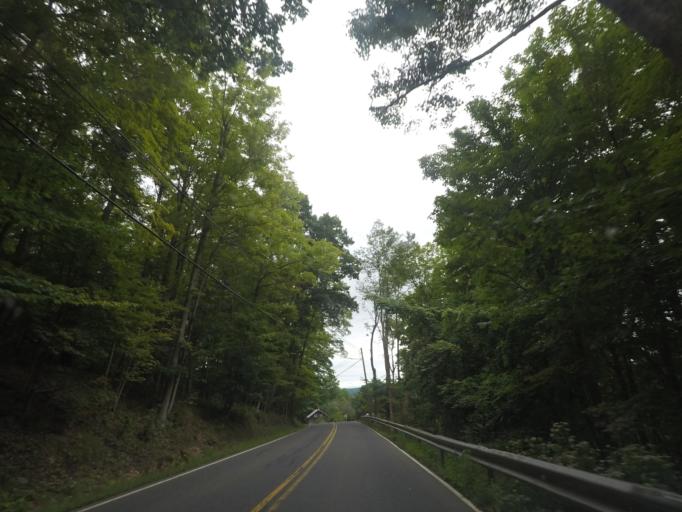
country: US
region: New York
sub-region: Rensselaer County
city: Nassau
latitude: 42.4728
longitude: -73.5899
